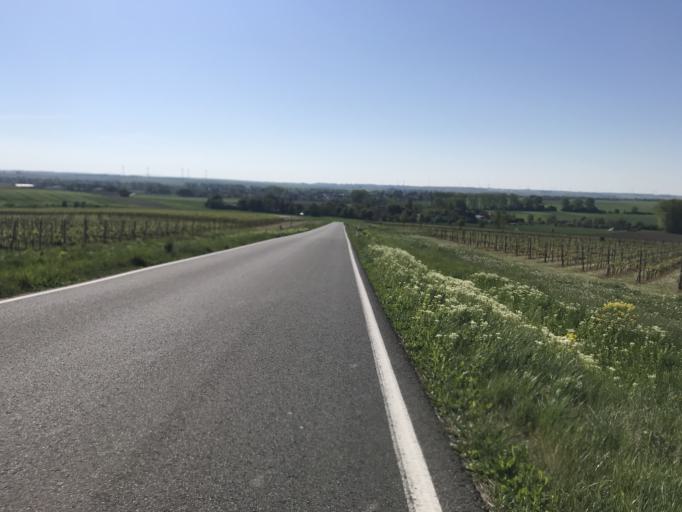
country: DE
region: Rheinland-Pfalz
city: Zornheim
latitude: 49.8715
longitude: 8.2208
